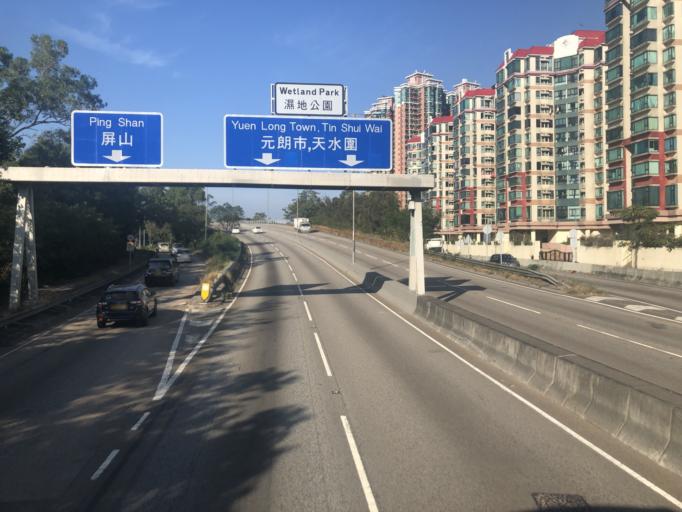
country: HK
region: Yuen Long
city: Yuen Long Kau Hui
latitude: 22.4420
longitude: 114.0165
